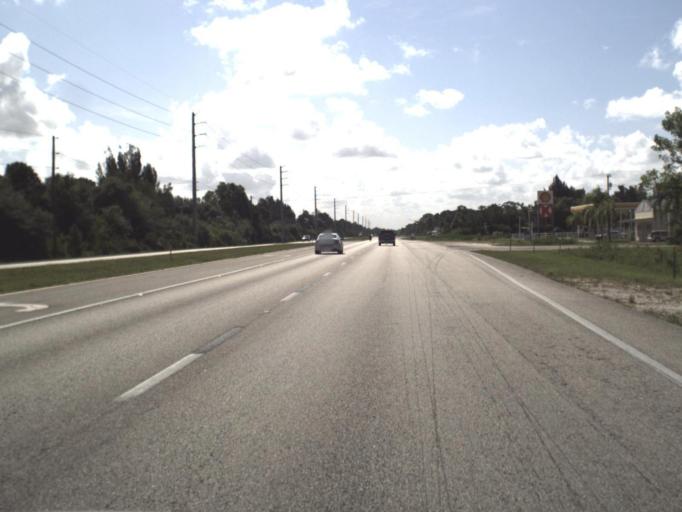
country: US
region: Florida
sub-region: Charlotte County
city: Charlotte Park
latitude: 26.8711
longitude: -82.0029
